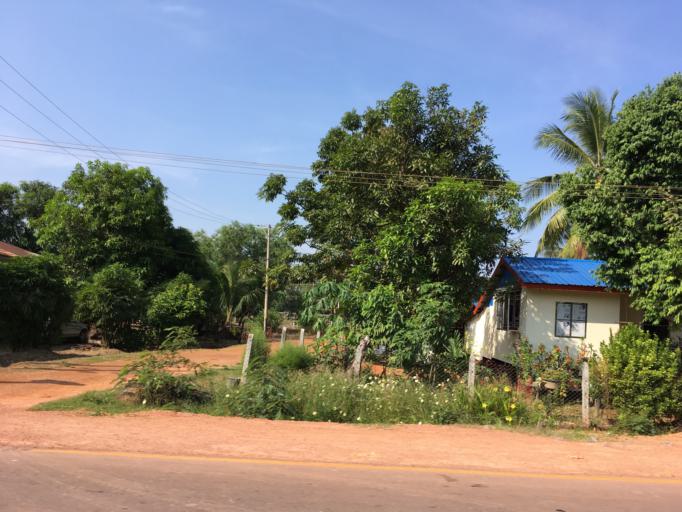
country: MM
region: Mon
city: Martaban
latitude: 16.6669
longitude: 97.7427
